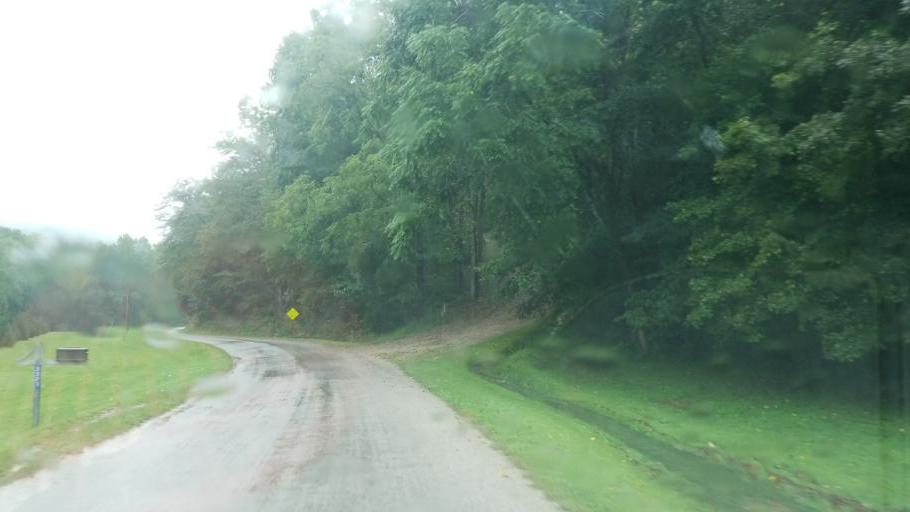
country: US
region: Kentucky
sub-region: Lewis County
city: Vanceburg
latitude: 38.7998
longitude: -83.2550
